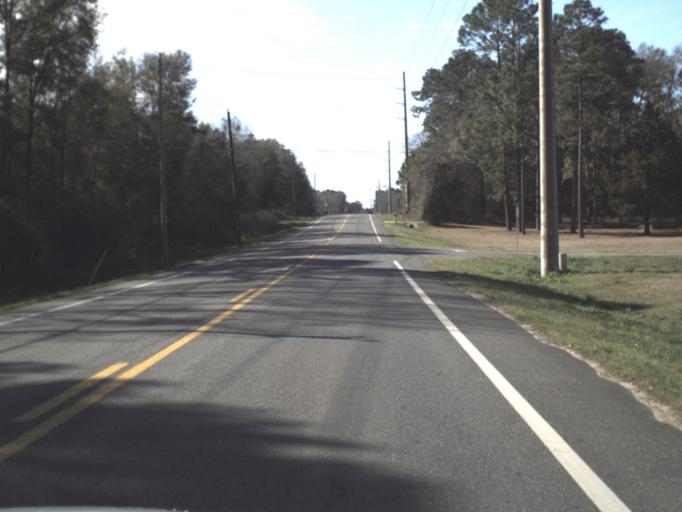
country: US
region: Florida
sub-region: Jackson County
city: Marianna
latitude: 30.7968
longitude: -85.1817
